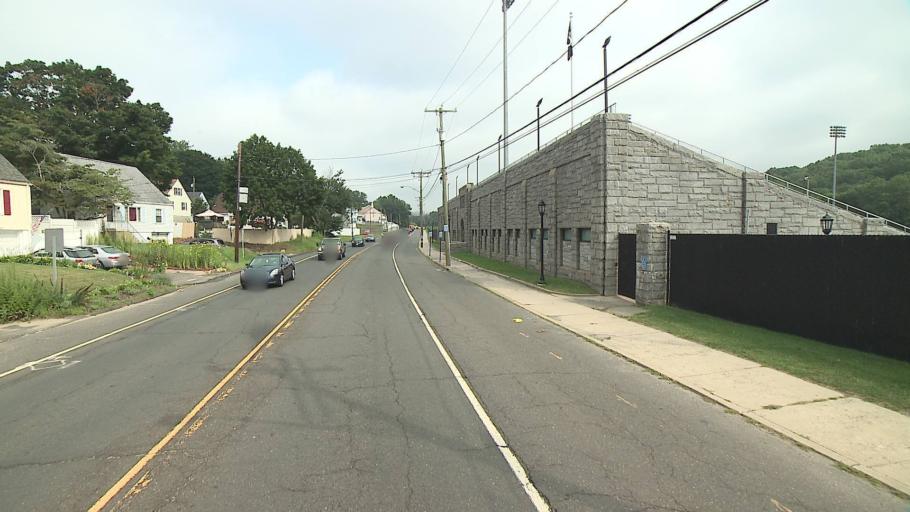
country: US
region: Connecticut
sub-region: Litchfield County
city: Oakville
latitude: 41.5770
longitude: -73.0704
